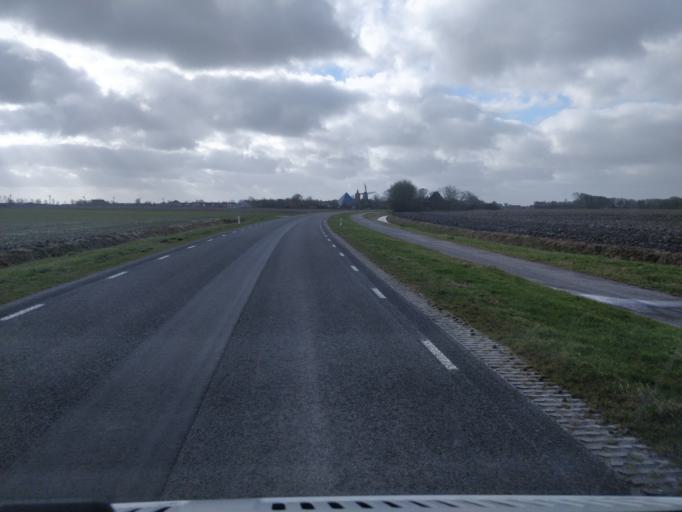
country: NL
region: Friesland
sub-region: Gemeente Franekeradeel
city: Sexbierum
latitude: 53.2262
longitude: 5.4951
